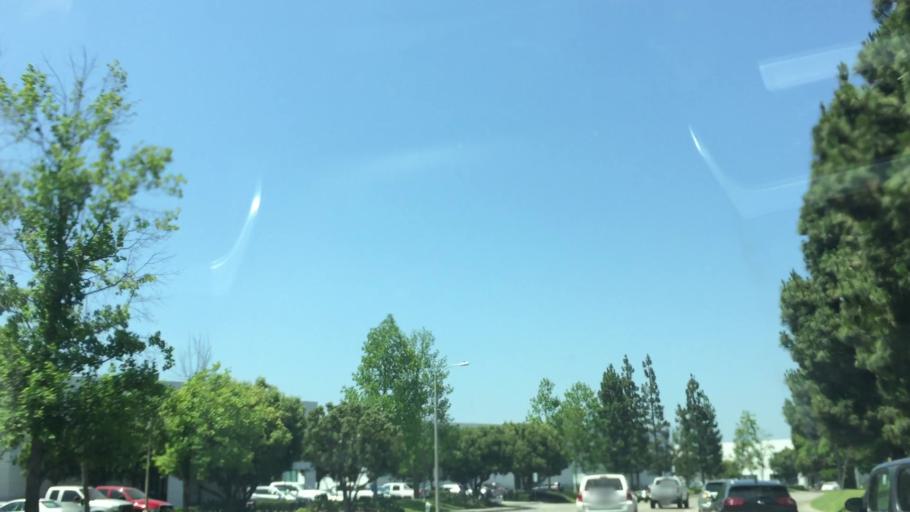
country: US
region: California
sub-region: Orange County
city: Fountain Valley
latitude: 33.7062
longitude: -117.9292
